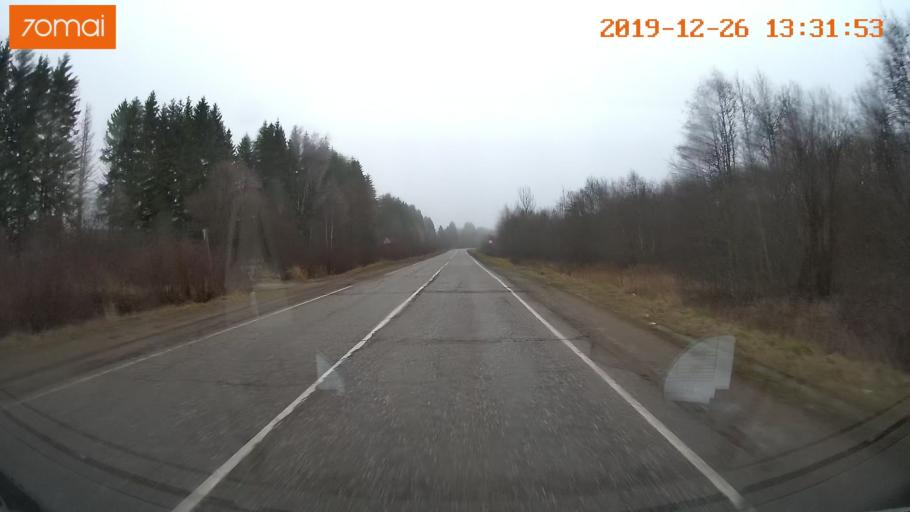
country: RU
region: Vologda
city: Sheksna
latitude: 58.8337
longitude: 38.2791
